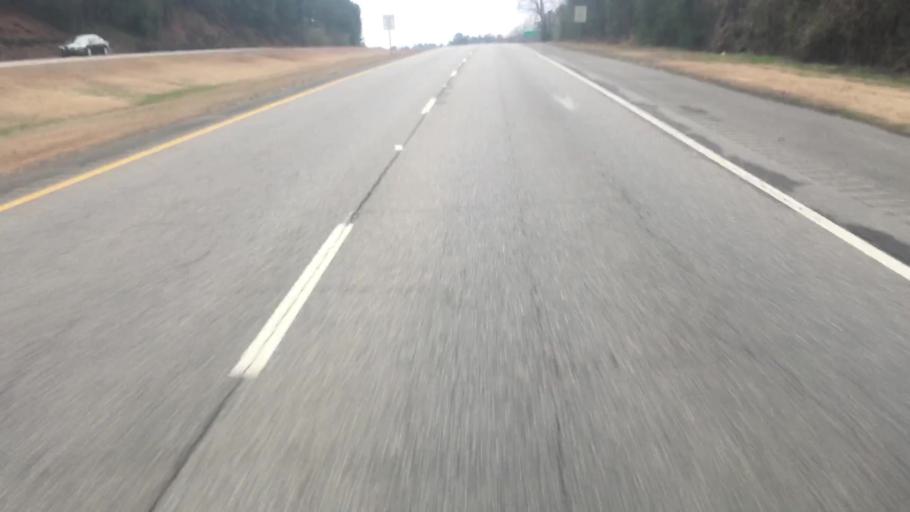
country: US
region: Alabama
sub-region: Walker County
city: Sumiton
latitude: 33.7663
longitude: -87.0703
